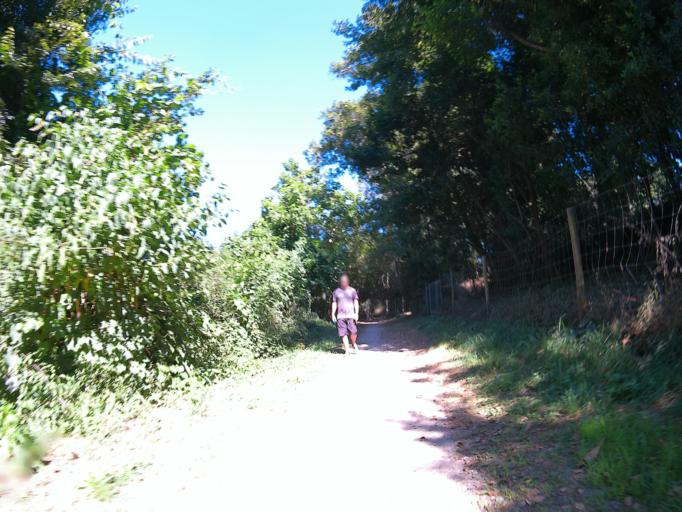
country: PT
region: Viana do Castelo
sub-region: Ponte de Lima
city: Ponte de Lima
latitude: 41.7613
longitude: -8.6000
